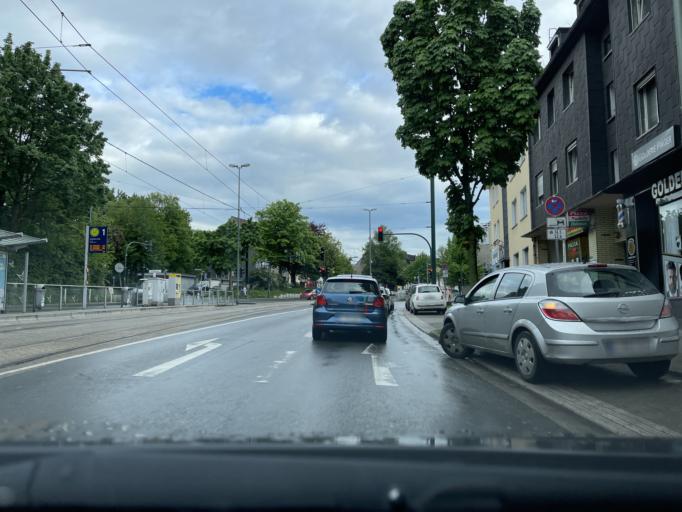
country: DE
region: North Rhine-Westphalia
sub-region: Regierungsbezirk Dusseldorf
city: Essen
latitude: 51.4769
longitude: 6.9783
